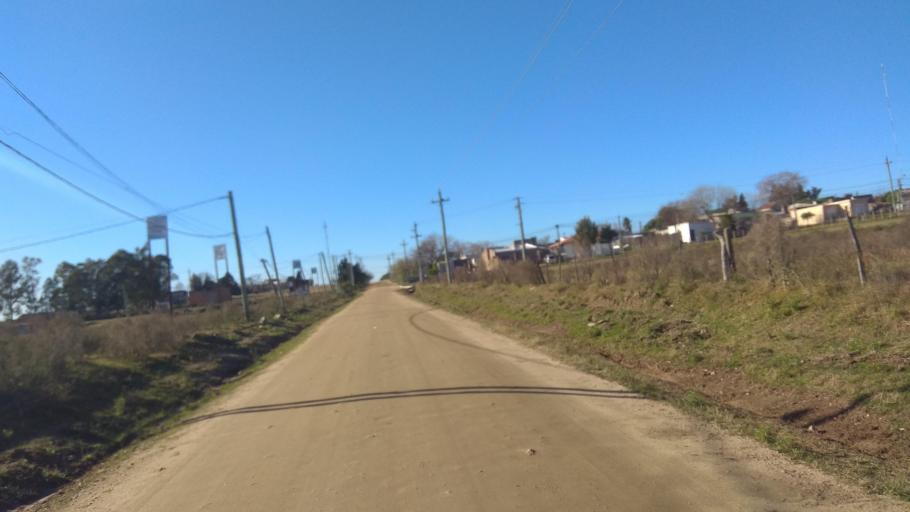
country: UY
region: Florida
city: Florida
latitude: -34.0844
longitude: -56.2411
